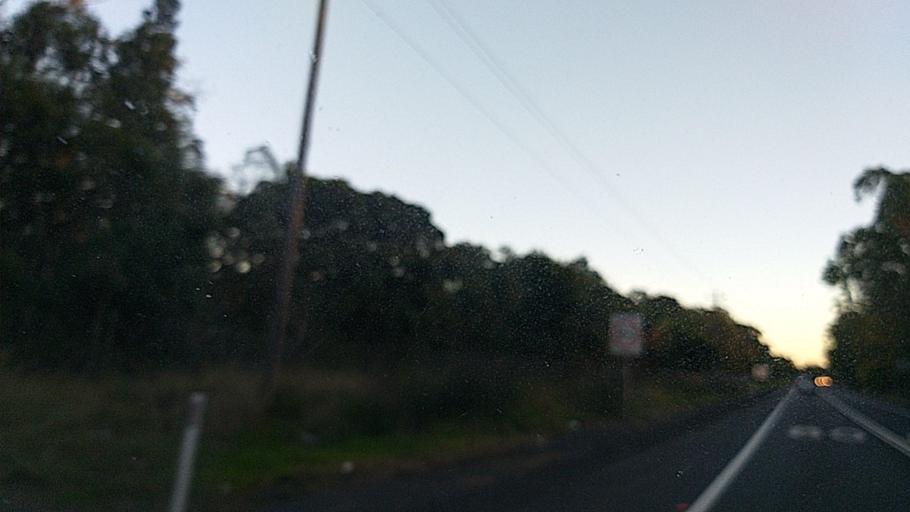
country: AU
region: New South Wales
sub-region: Hawkesbury
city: South Windsor
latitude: -33.6575
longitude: 150.7952
